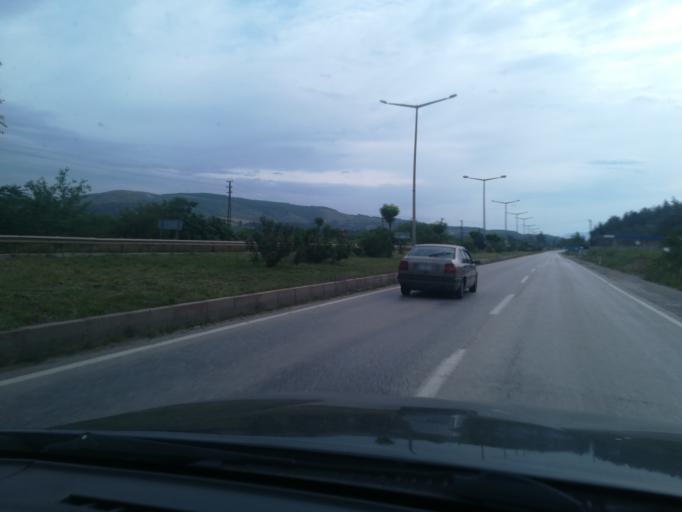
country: TR
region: Osmaniye
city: Toprakkale
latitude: 37.0536
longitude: 36.1590
